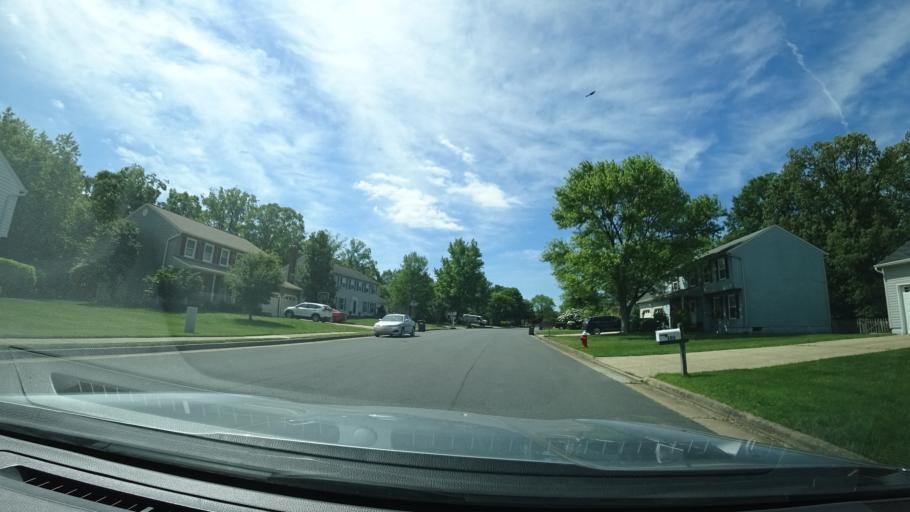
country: US
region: Virginia
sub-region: Loudoun County
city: Oak Grove
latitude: 38.9869
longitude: -77.4021
